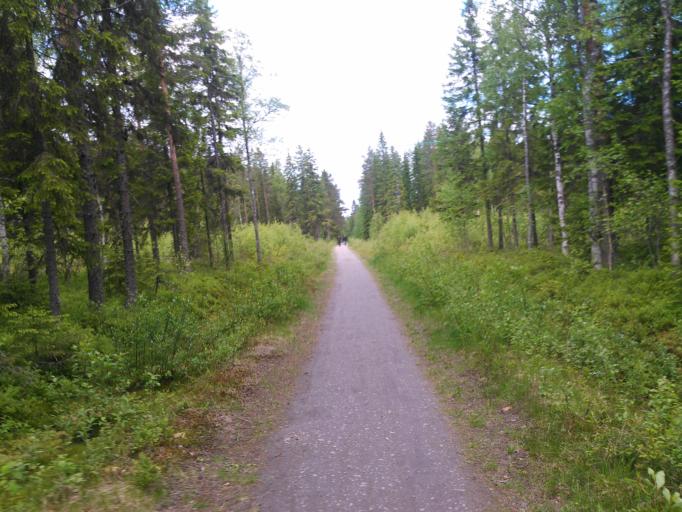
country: SE
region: Vaesterbotten
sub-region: Umea Kommun
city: Ersmark
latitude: 63.8658
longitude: 20.3337
